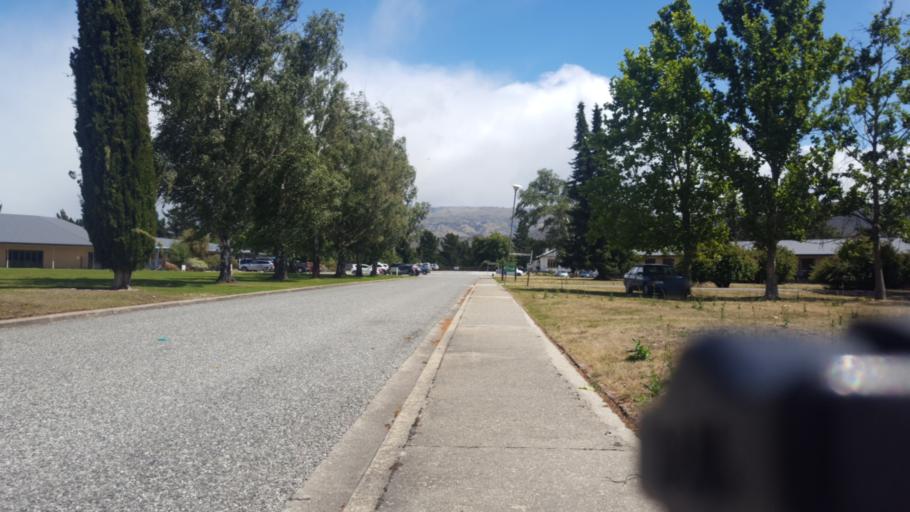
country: NZ
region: Otago
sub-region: Queenstown-Lakes District
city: Wanaka
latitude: -45.1999
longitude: 169.3307
